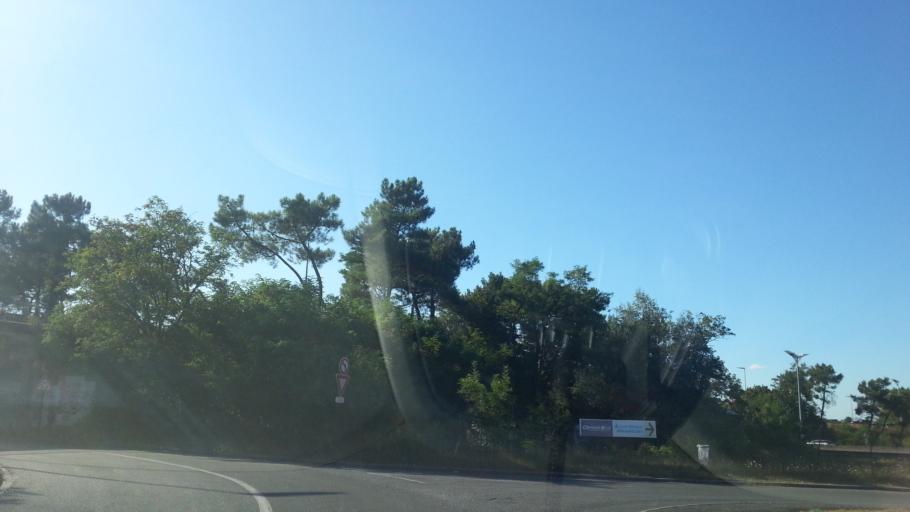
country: FR
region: Aquitaine
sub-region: Departement de la Gironde
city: Villenave-d'Ornon
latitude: 44.7771
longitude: -0.5652
